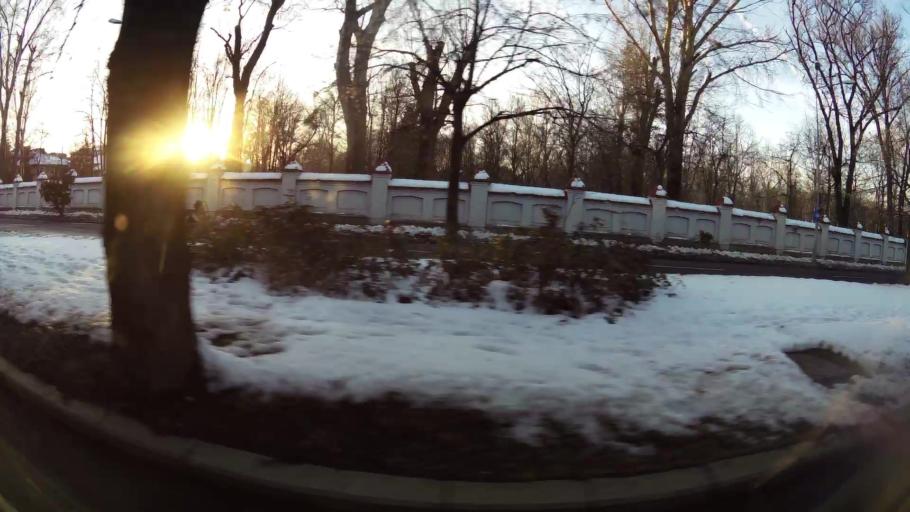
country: RO
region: Bucuresti
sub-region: Municipiul Bucuresti
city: Bucuresti
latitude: 44.4336
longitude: 26.0669
